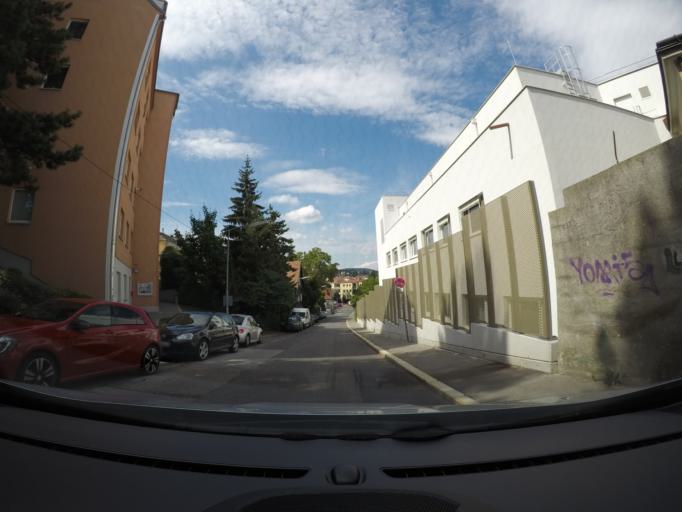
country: AT
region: Lower Austria
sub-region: Politischer Bezirk Modling
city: Perchtoldsdorf
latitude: 48.1940
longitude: 16.2616
